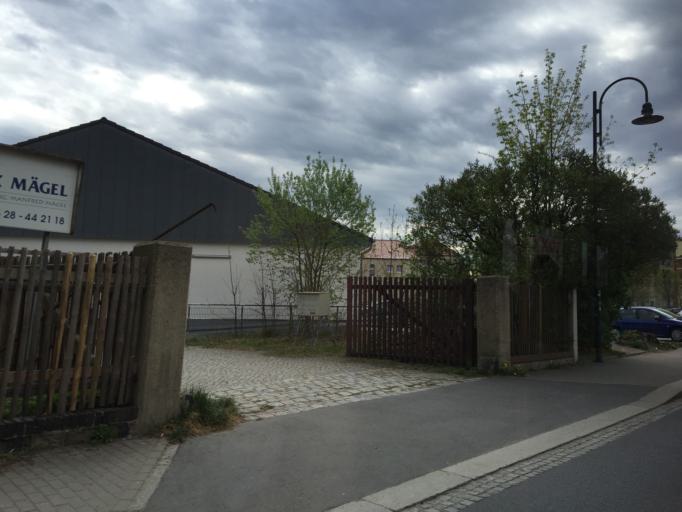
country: DE
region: Saxony
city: Radeberg
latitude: 51.1126
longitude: 13.9174
